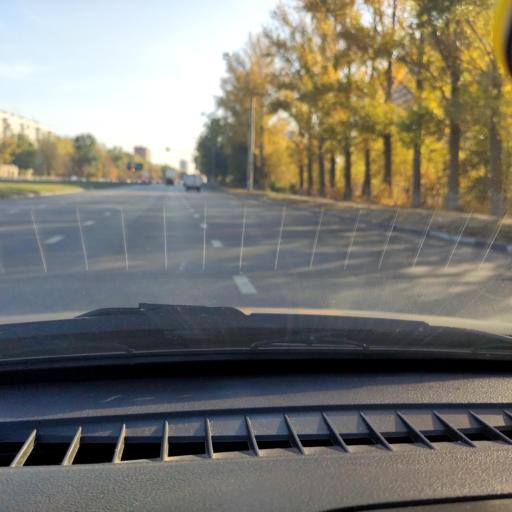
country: RU
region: Samara
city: Tol'yatti
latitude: 53.5202
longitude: 49.2585
